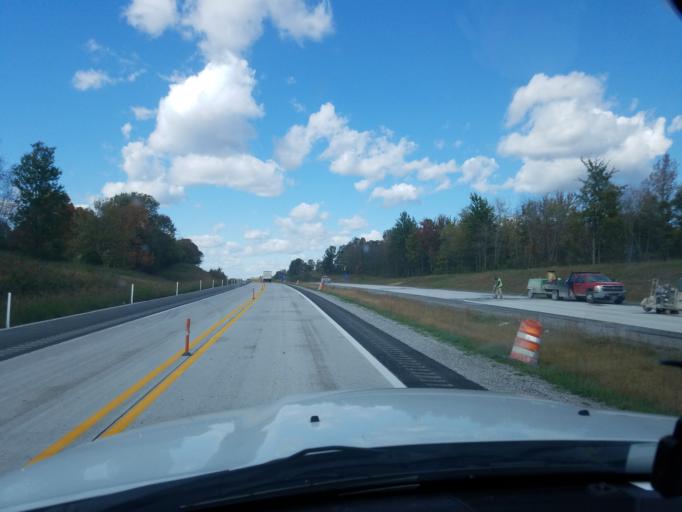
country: US
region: Kentucky
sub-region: Ohio County
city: Beaver Dam
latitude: 37.4429
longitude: -86.8608
